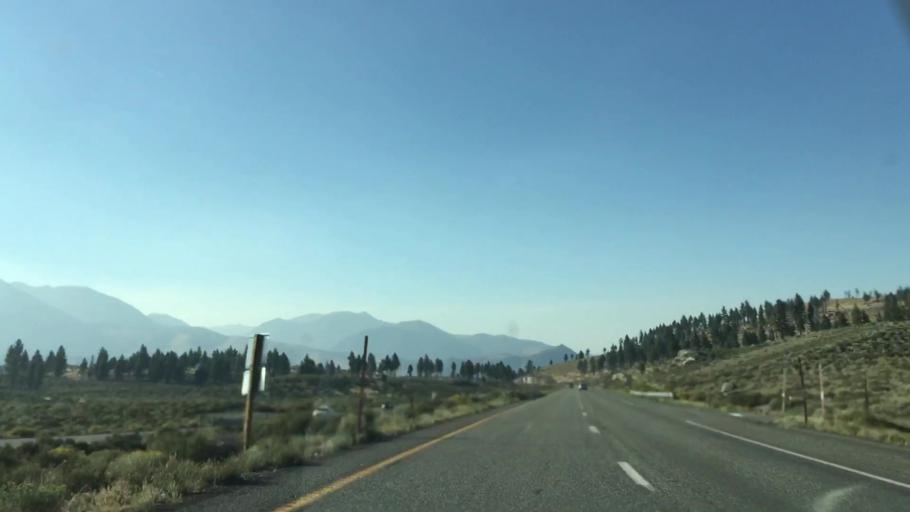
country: US
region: California
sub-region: Mono County
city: Mammoth Lakes
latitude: 37.8190
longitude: -119.0603
